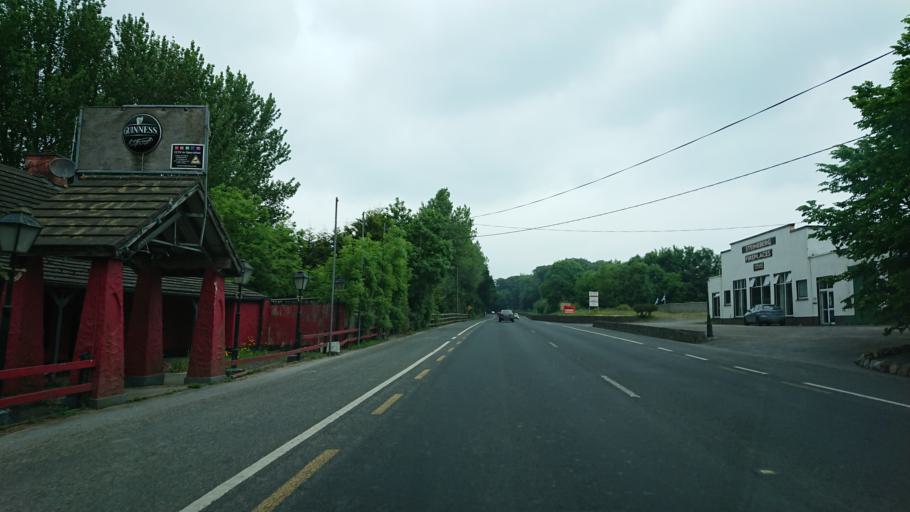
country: IE
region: Munster
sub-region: Waterford
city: Waterford
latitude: 52.2063
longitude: -7.1162
